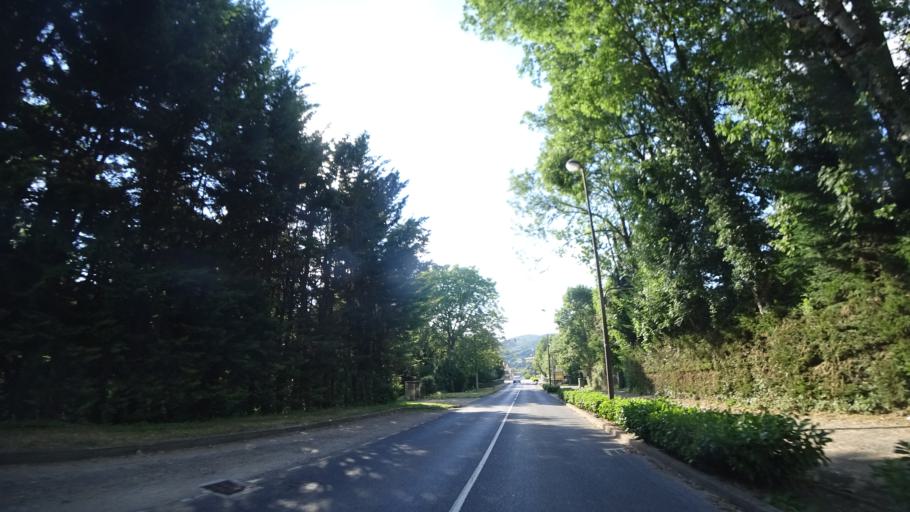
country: FR
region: Languedoc-Roussillon
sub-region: Departement de la Lozere
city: La Canourgue
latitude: 44.4357
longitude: 3.2029
